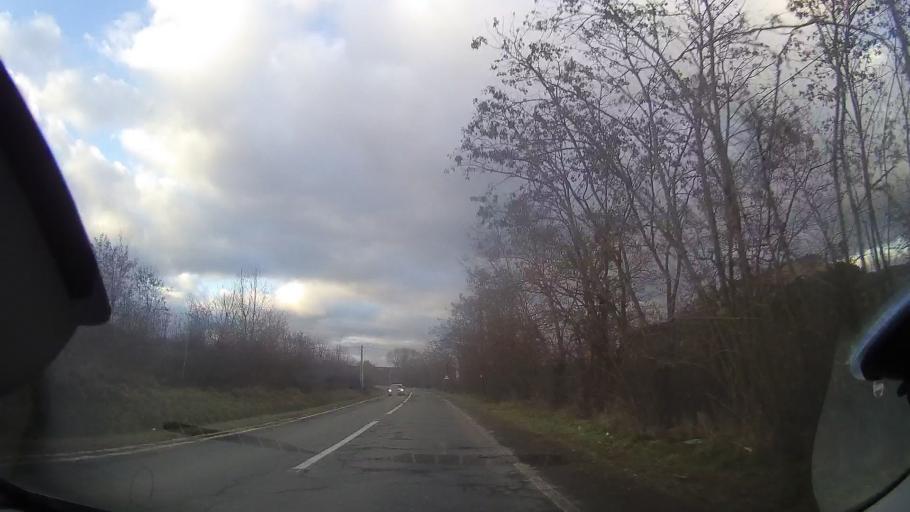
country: RO
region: Cluj
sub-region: Comuna Calatele
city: Calatele
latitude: 46.7844
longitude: 23.0038
